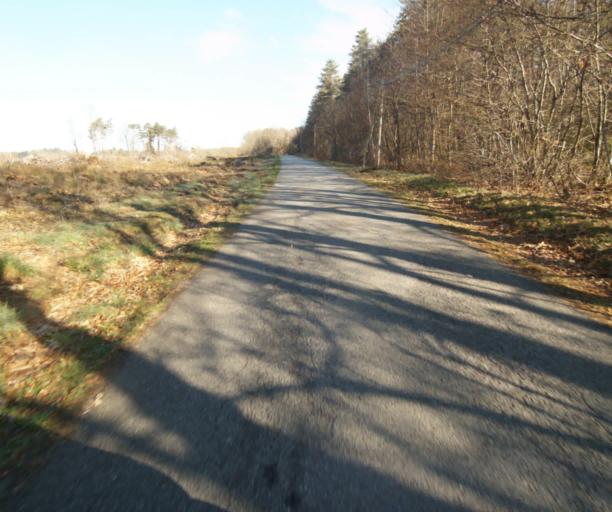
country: FR
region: Limousin
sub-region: Departement de la Correze
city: Correze
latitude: 45.3247
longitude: 1.8844
